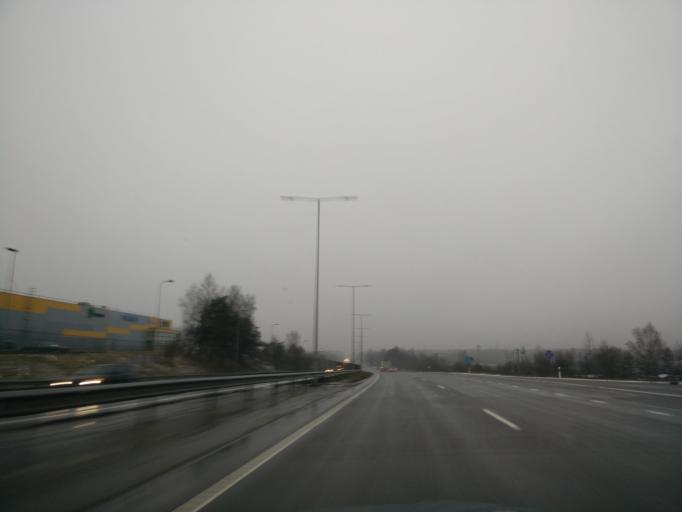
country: LT
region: Vilnius County
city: Pilaite
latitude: 54.6556
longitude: 25.1490
